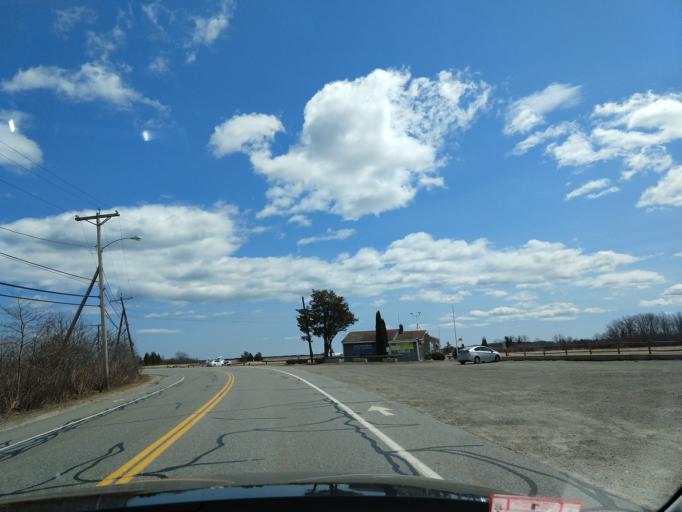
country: US
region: Massachusetts
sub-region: Essex County
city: Newburyport
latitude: 42.7963
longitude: -70.8418
